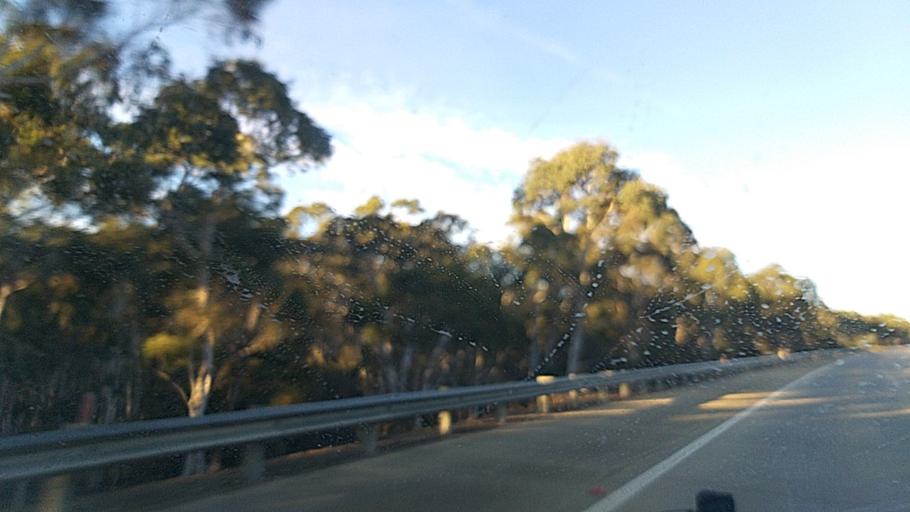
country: AU
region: New South Wales
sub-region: Yass Valley
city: Gundaroo
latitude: -35.1550
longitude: 149.3279
